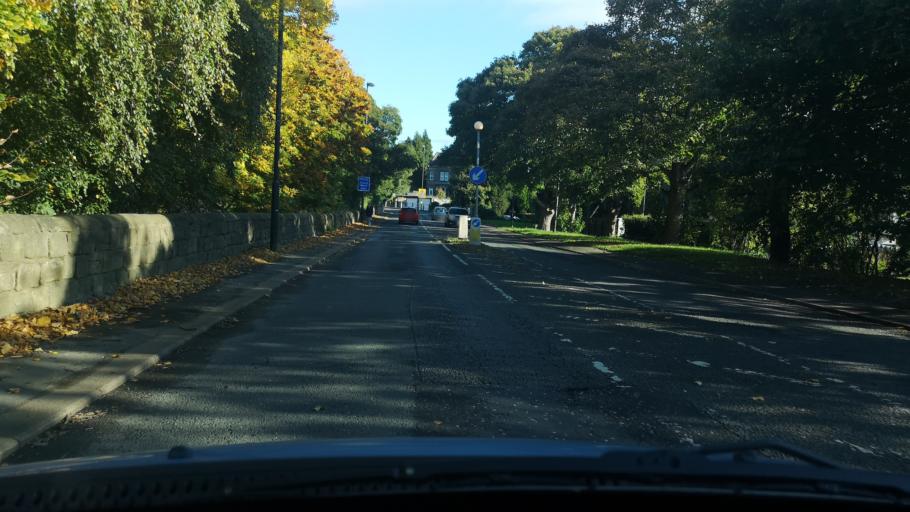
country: GB
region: England
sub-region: City and Borough of Wakefield
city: Low Ackworth
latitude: 53.6464
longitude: -1.3336
